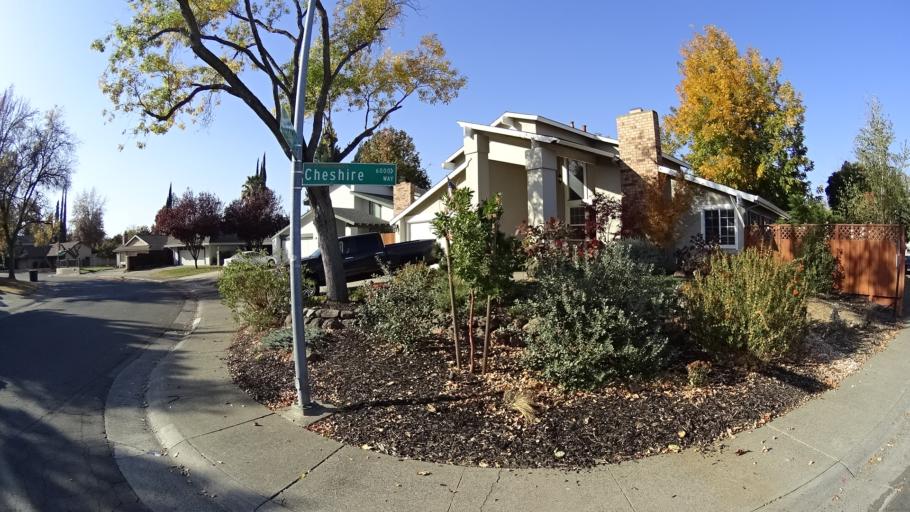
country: US
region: California
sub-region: Sacramento County
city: Citrus Heights
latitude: 38.6759
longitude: -121.2790
